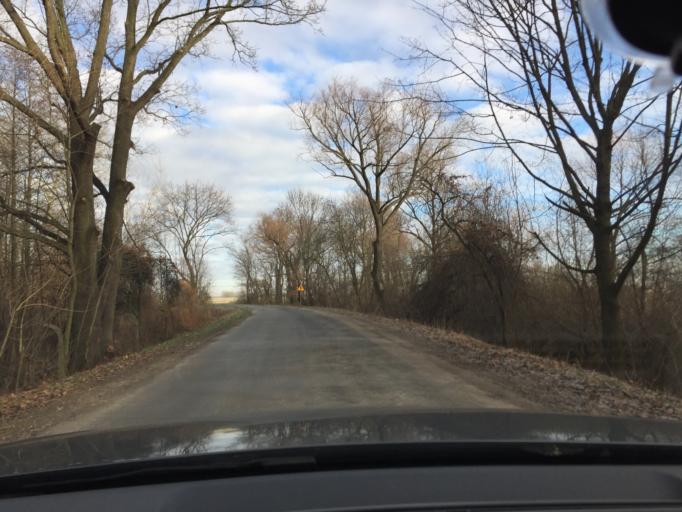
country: PL
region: Lower Silesian Voivodeship
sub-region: Powiat sredzki
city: Udanin
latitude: 51.0461
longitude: 16.5173
